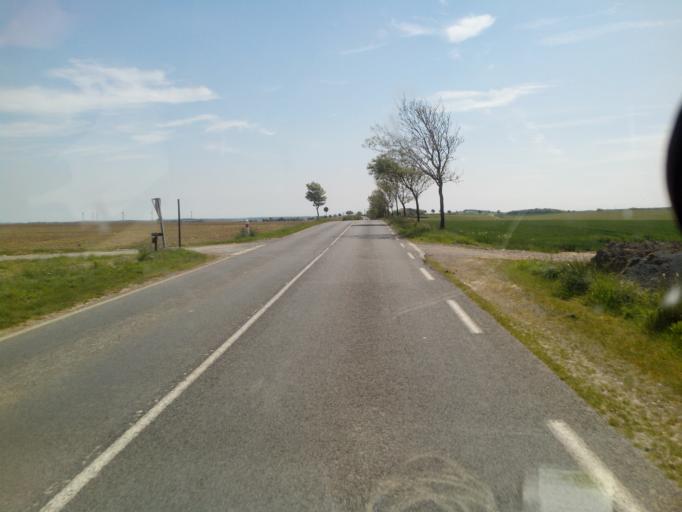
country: FR
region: Nord-Pas-de-Calais
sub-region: Departement du Pas-de-Calais
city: Samer
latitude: 50.5975
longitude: 1.7423
